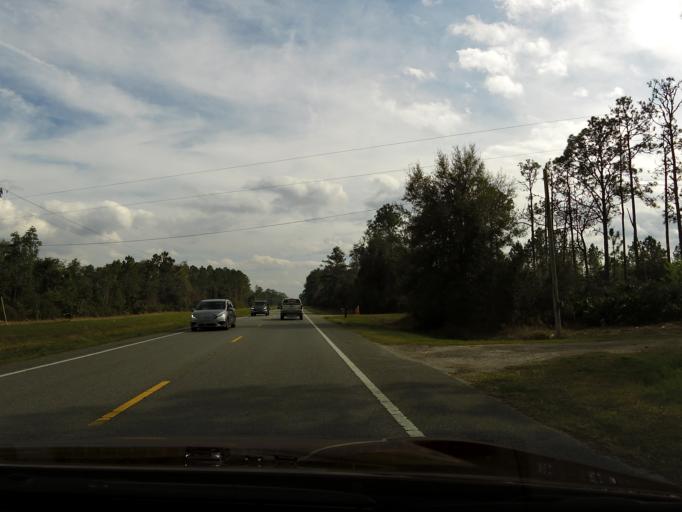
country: US
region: Florida
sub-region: Volusia County
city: De Leon Springs
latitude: 29.1934
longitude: -81.3121
